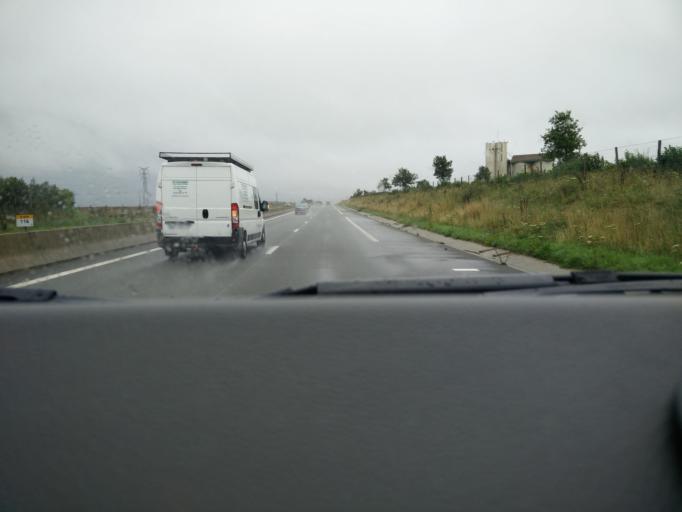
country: FR
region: Nord-Pas-de-Calais
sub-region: Departement du Pas-de-Calais
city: Marconnelle
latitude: 50.3678
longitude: 1.9569
